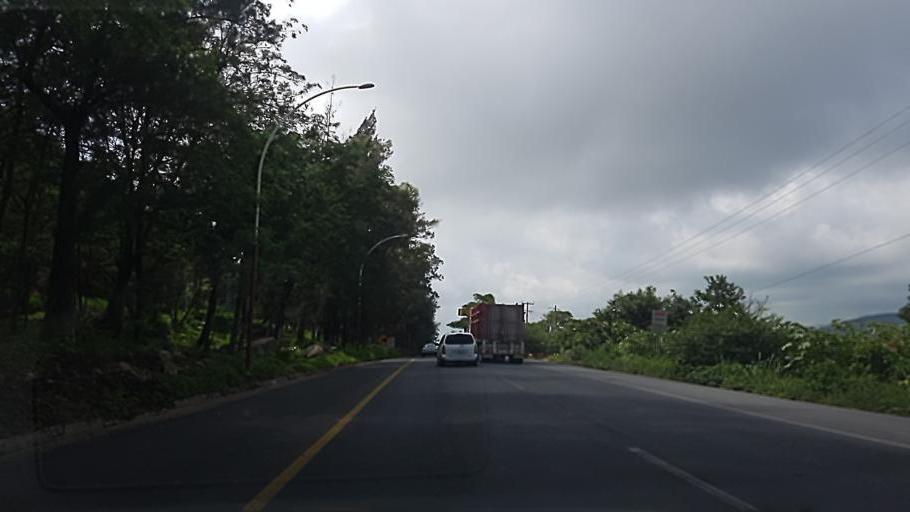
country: MX
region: Nayarit
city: Tepic
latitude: 21.5067
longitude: -104.9213
